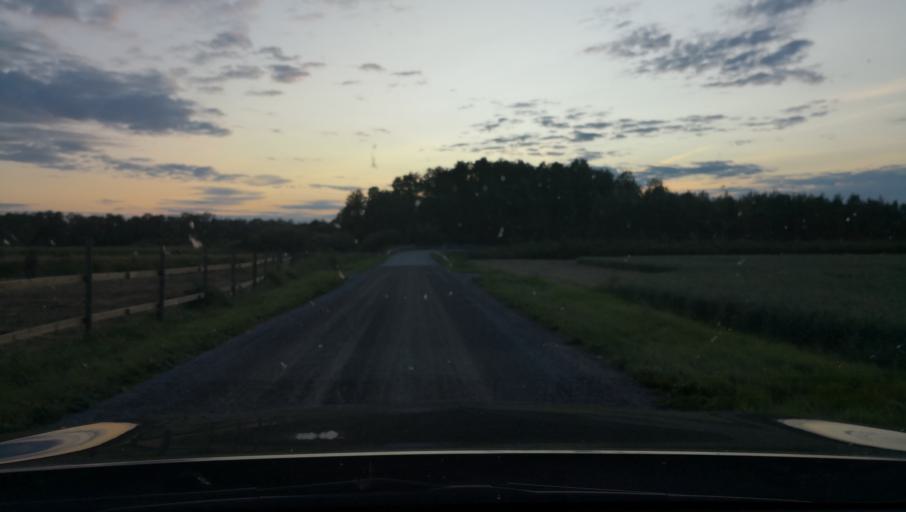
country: SE
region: Uppsala
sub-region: Osthammars Kommun
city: Bjorklinge
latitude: 60.0603
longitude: 17.5824
